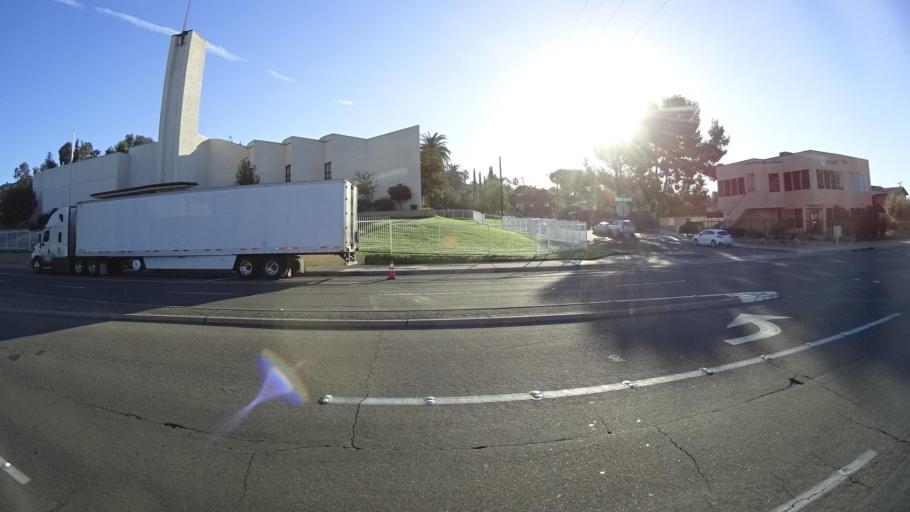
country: US
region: California
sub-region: San Diego County
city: Bostonia
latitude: 32.8156
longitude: -116.9358
